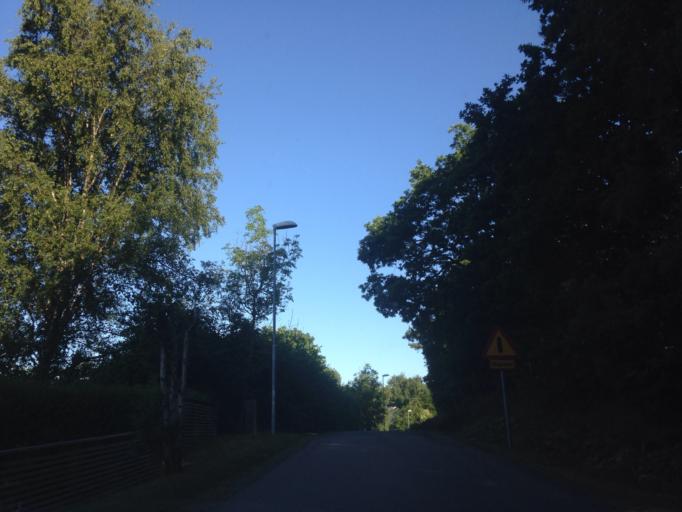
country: SE
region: Vaestra Goetaland
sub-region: Goteborg
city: Torslanda
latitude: 57.7698
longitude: 11.8500
